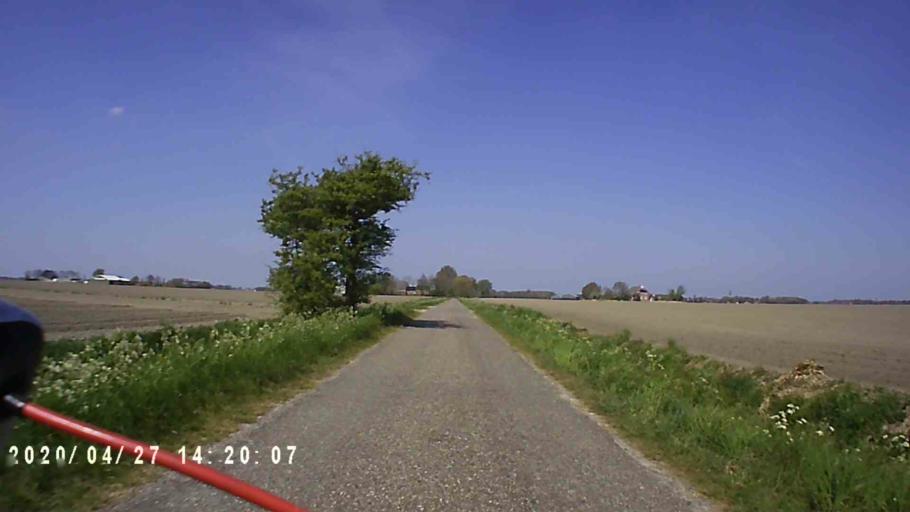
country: NL
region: Groningen
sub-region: Gemeente De Marne
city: Ulrum
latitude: 53.3701
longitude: 6.3836
